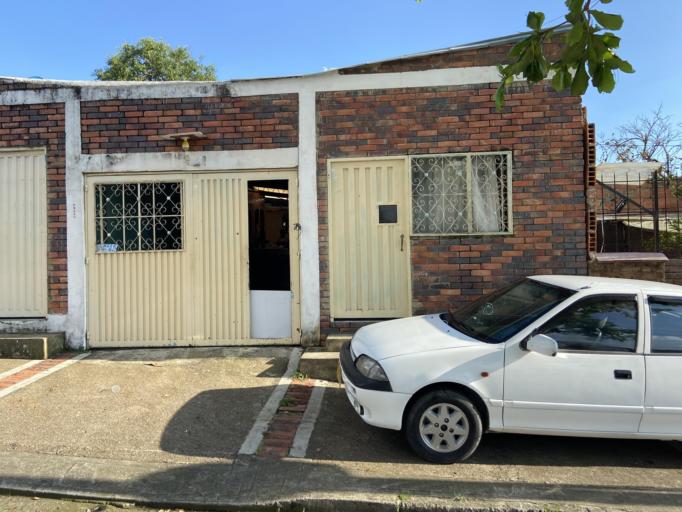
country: CO
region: Cundinamarca
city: San Antonio del Tequendama
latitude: 4.6315
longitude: -74.4596
